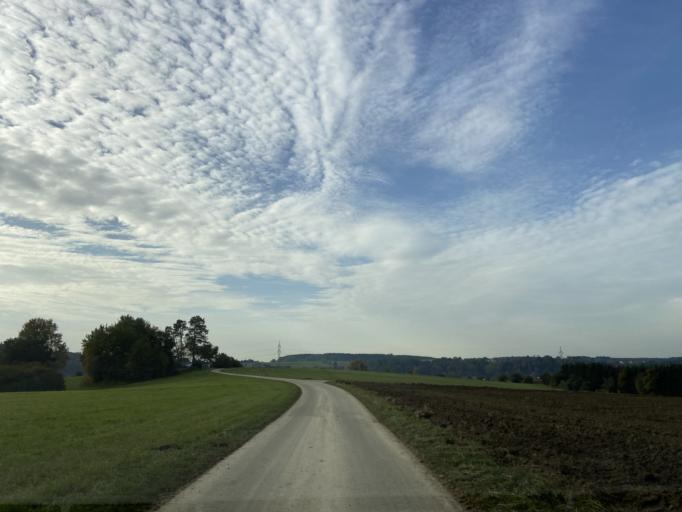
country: DE
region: Baden-Wuerttemberg
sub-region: Tuebingen Region
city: Bingen
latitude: 48.1153
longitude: 9.2892
